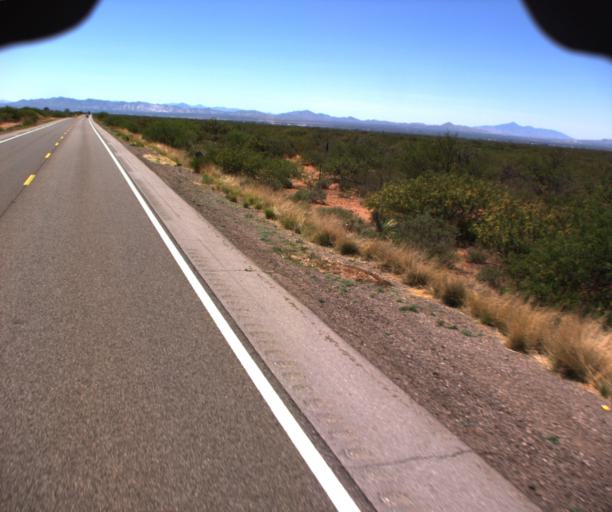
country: US
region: Arizona
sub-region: Cochise County
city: Douglas
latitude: 31.4226
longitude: -109.4891
